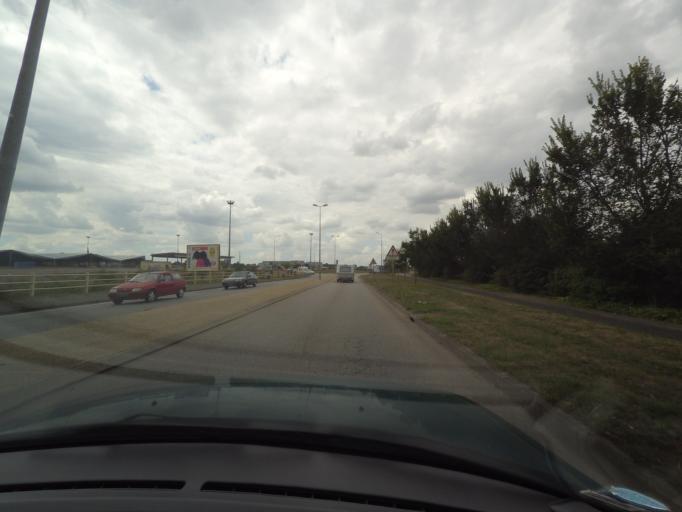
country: FR
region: Poitou-Charentes
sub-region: Departement des Deux-Sevres
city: Chatillon-sur-Thouet
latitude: 46.6538
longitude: -0.2342
